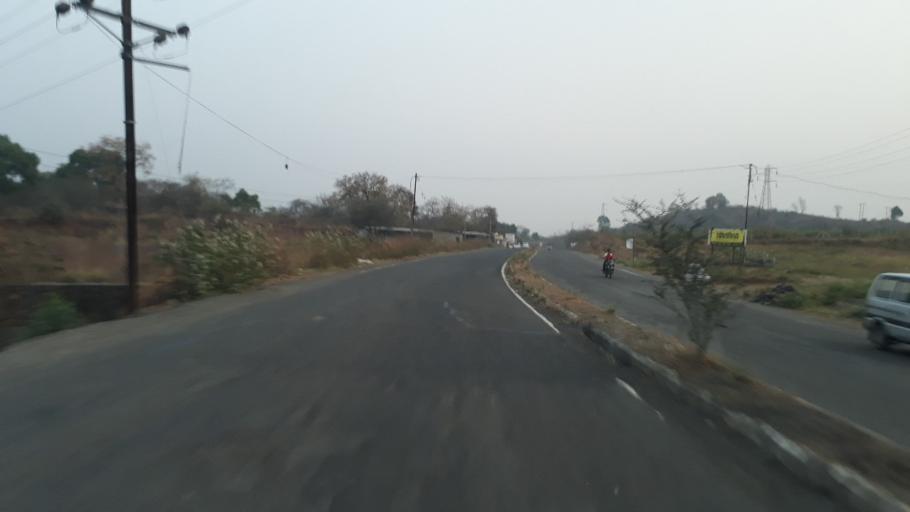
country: IN
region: Maharashtra
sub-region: Raigarh
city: Neral
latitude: 19.0133
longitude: 73.3251
